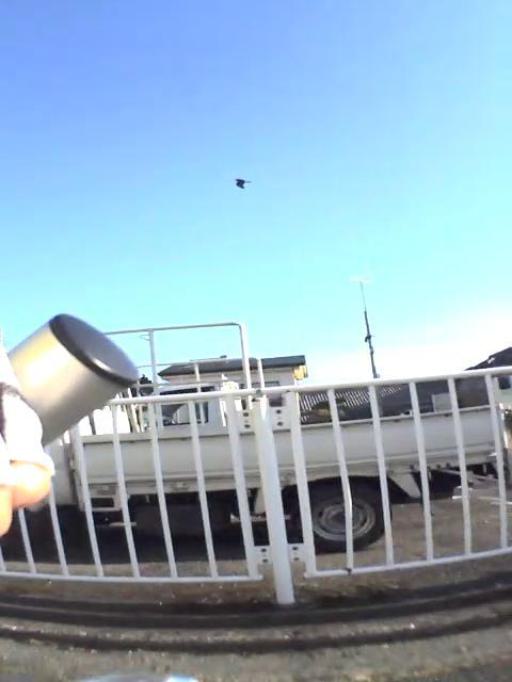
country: JP
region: Yamaguchi
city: Nagato
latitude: 34.3896
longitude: 131.1991
